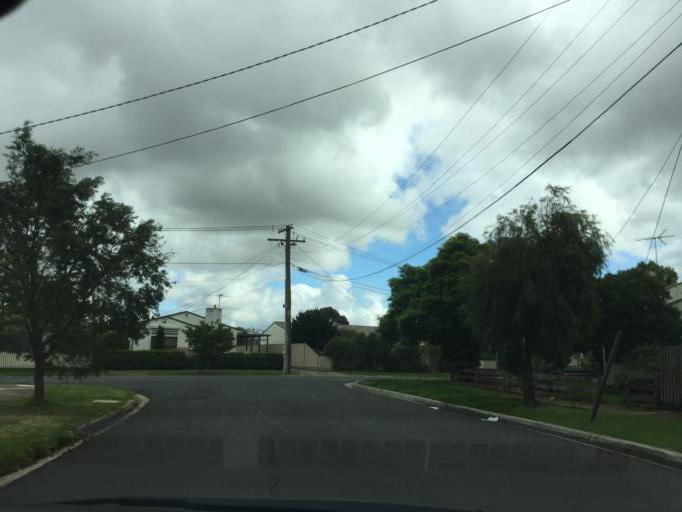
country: AU
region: Victoria
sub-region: Brimbank
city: Sunshine North
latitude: -37.7803
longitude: 144.8241
